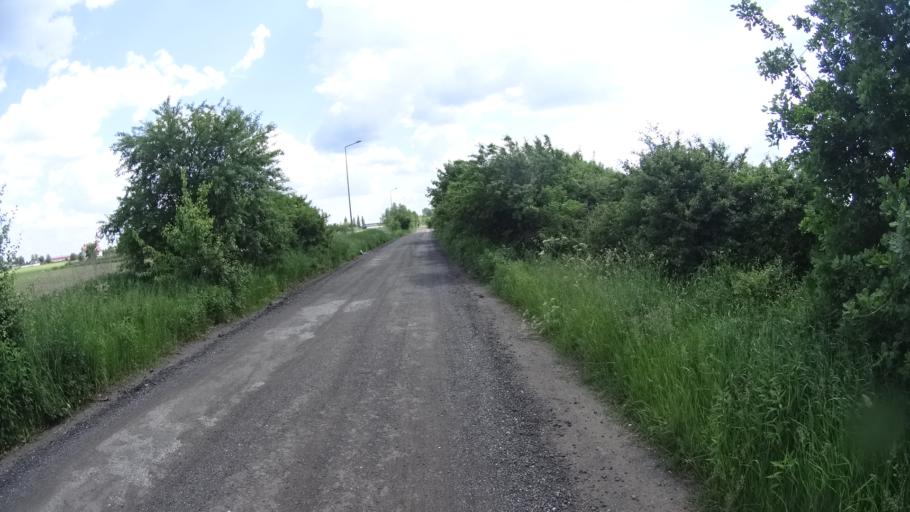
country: PL
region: Masovian Voivodeship
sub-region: Powiat pruszkowski
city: Nadarzyn
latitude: 52.0582
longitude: 20.8233
